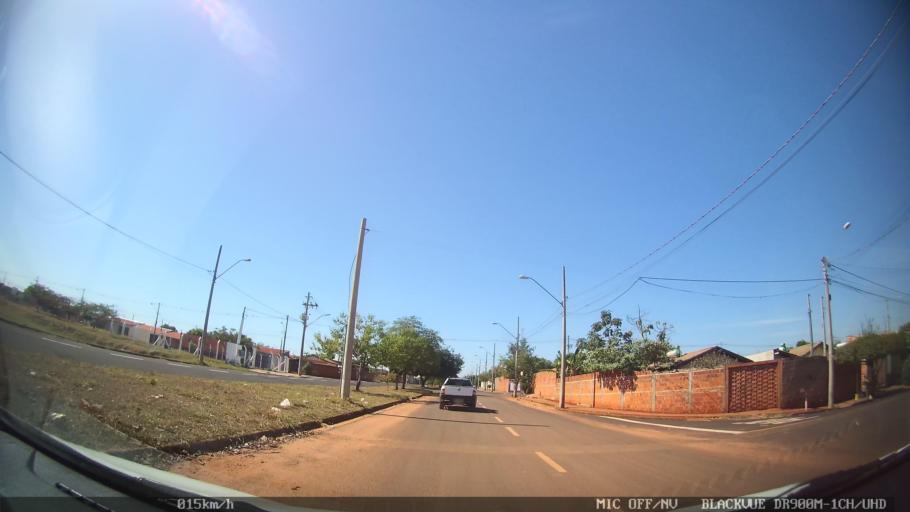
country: BR
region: Sao Paulo
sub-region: Sao Jose Do Rio Preto
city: Sao Jose do Rio Preto
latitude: -20.7404
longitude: -49.4205
